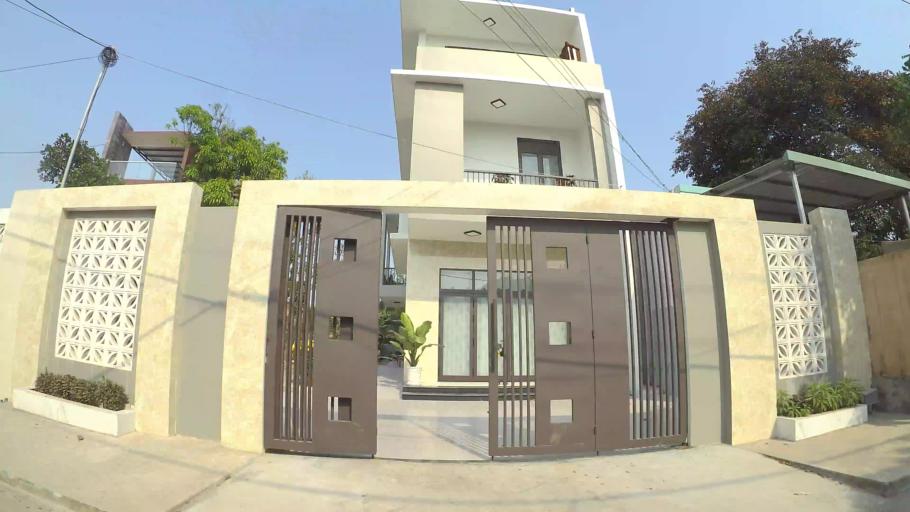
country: VN
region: Da Nang
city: Cam Le
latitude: 16.0150
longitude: 108.1866
